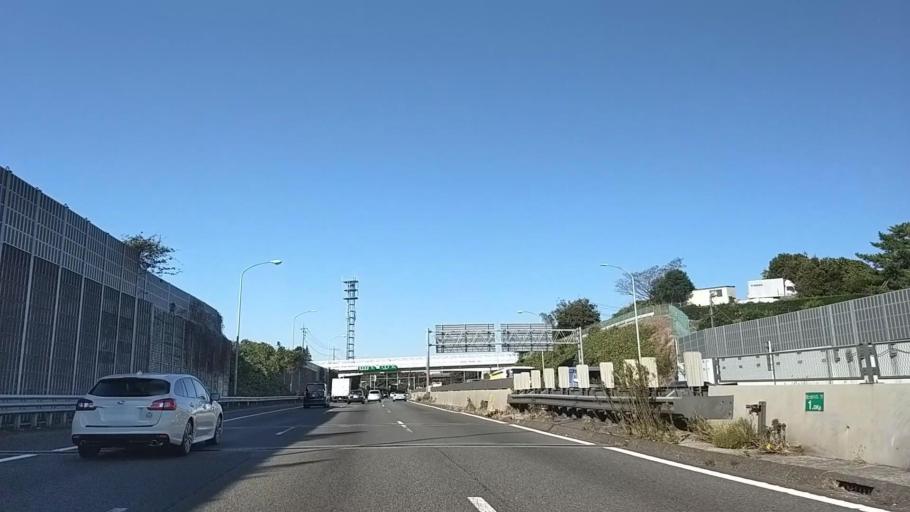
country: JP
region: Kanagawa
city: Yokohama
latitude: 35.4535
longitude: 139.5574
